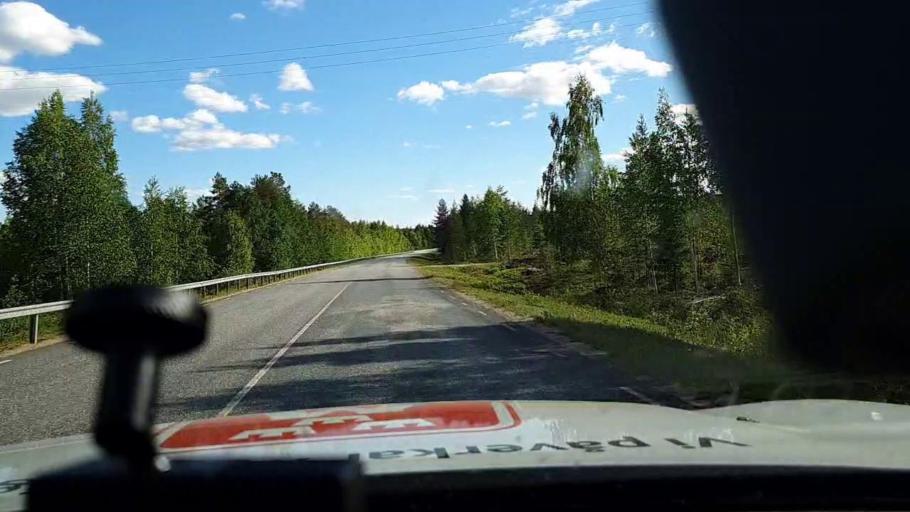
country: SE
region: Norrbotten
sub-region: Overtornea Kommun
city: OEvertornea
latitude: 66.3463
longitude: 23.6483
